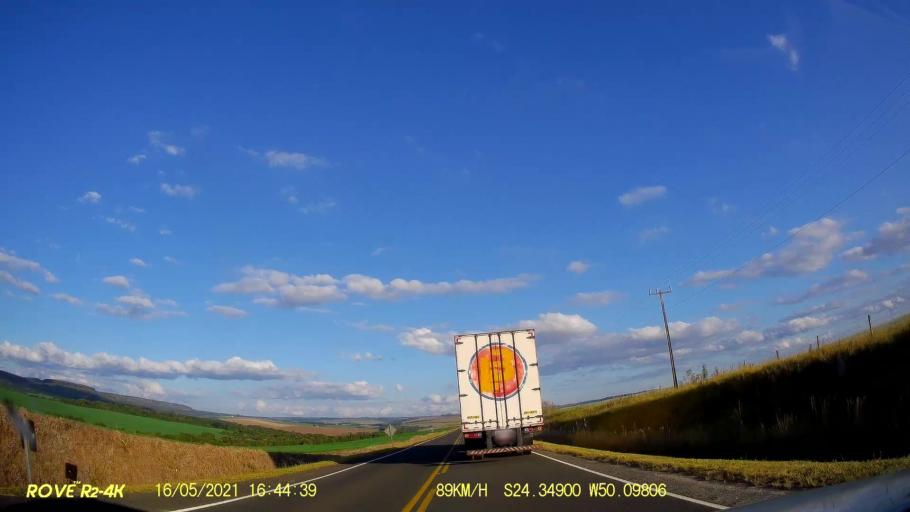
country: BR
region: Parana
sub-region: Pirai Do Sul
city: Pirai do Sul
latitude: -24.3494
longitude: -50.0979
